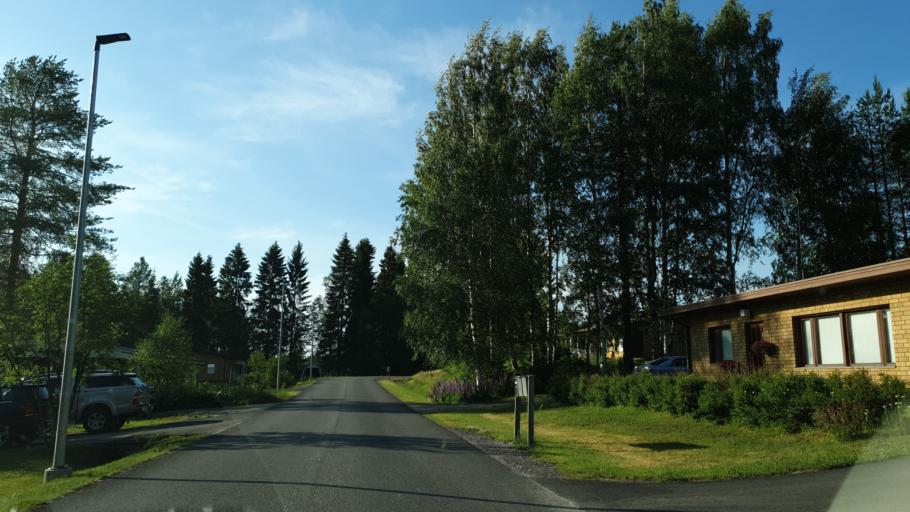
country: FI
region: Kainuu
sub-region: Kehys-Kainuu
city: Kuhmo
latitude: 64.1184
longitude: 29.4942
